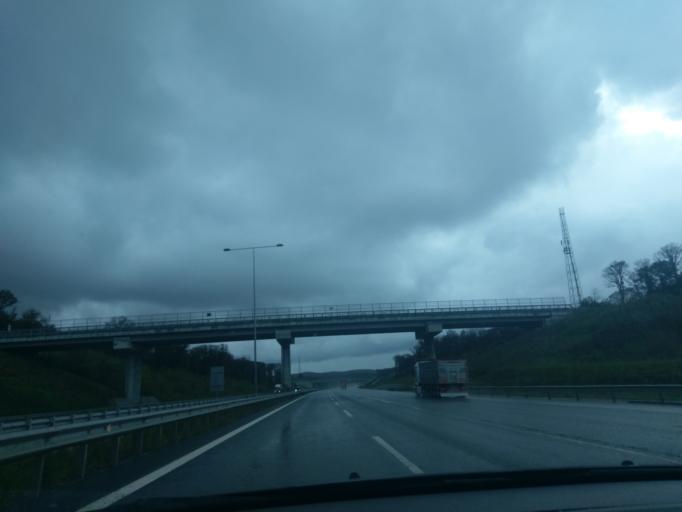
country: TR
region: Istanbul
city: Kemerburgaz
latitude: 41.2342
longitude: 28.9179
